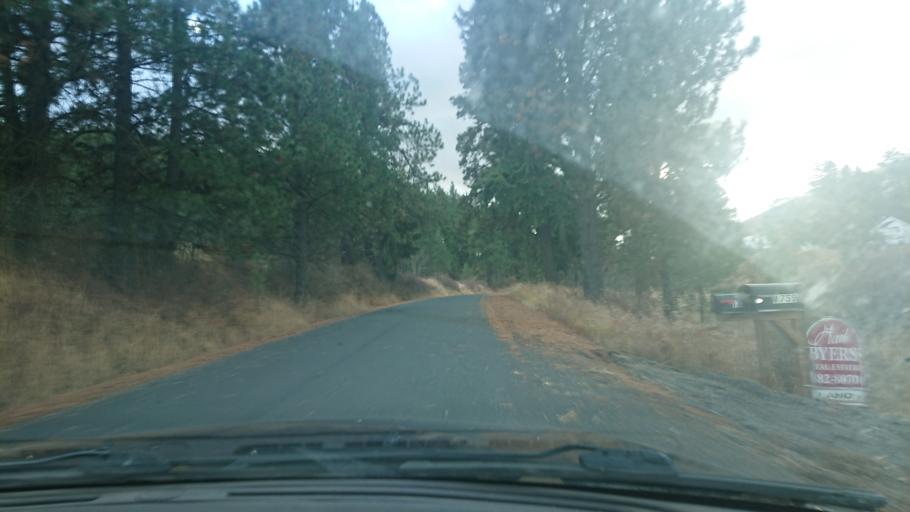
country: US
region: Idaho
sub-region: Latah County
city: Moscow
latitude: 46.7000
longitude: -116.8619
